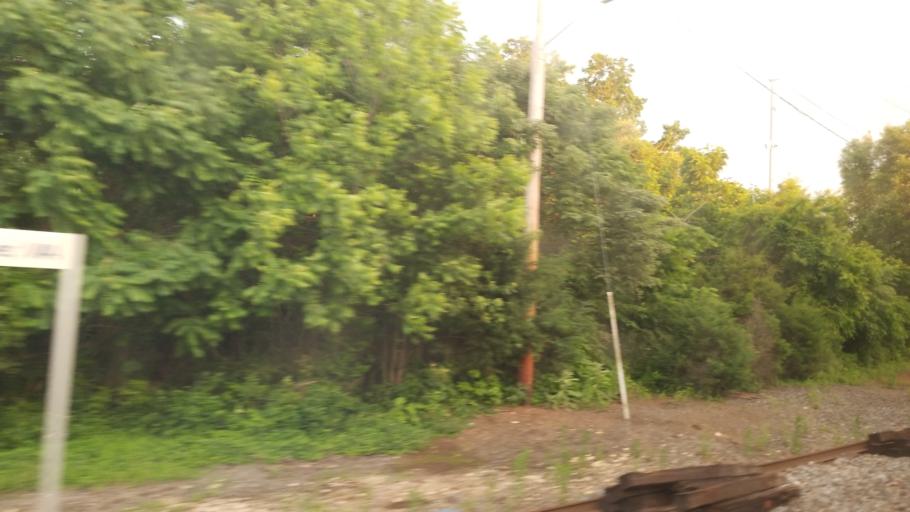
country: US
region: Virginia
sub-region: Culpeper County
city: Culpeper
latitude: 38.4725
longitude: -77.9927
